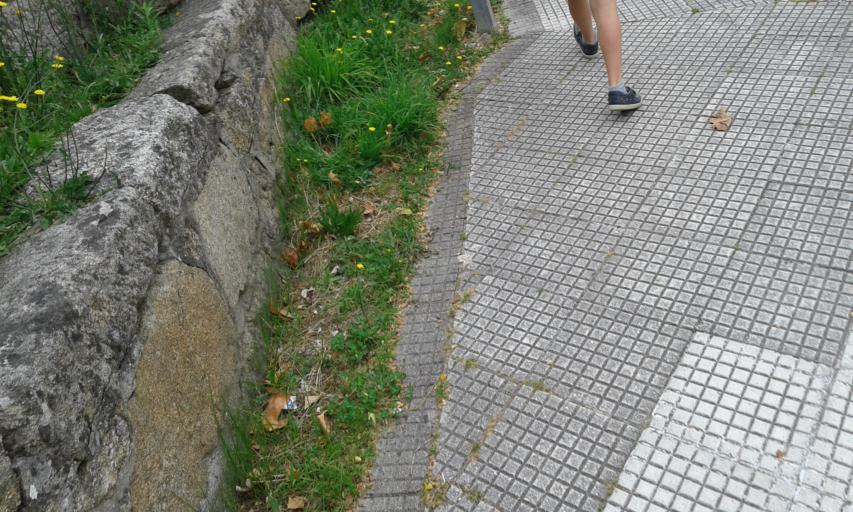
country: ES
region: Galicia
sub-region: Provincia de Pontevedra
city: Gondomar
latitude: 42.1123
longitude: -8.7638
